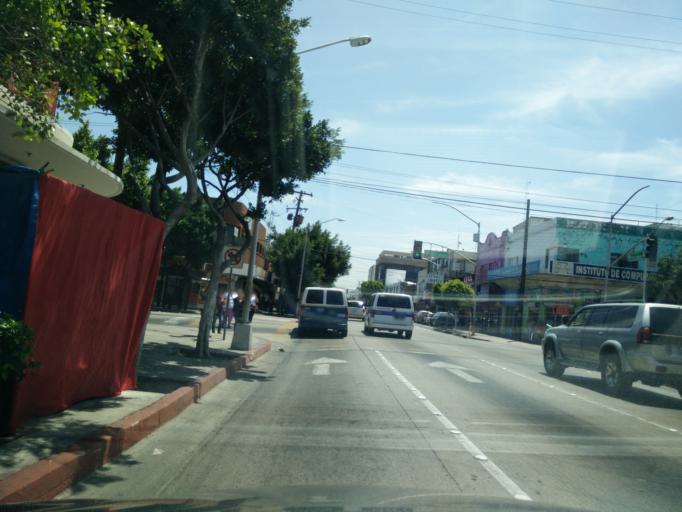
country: MX
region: Baja California
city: Tijuana
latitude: 32.5325
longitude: -117.0401
